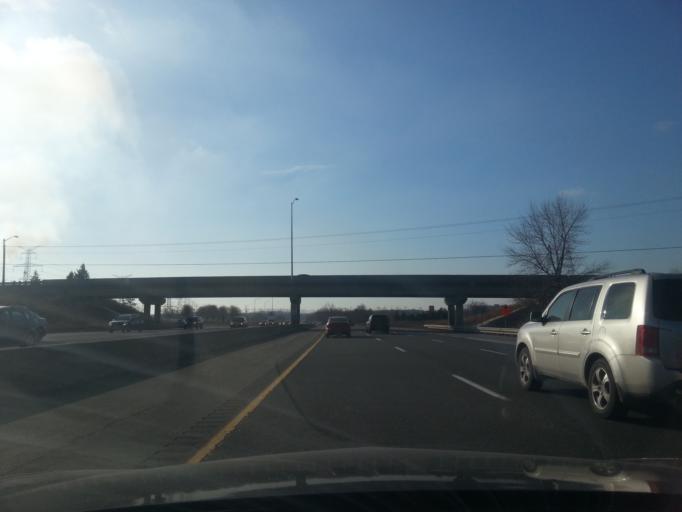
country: CA
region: Ontario
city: Oshawa
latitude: 43.8950
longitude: -78.6885
